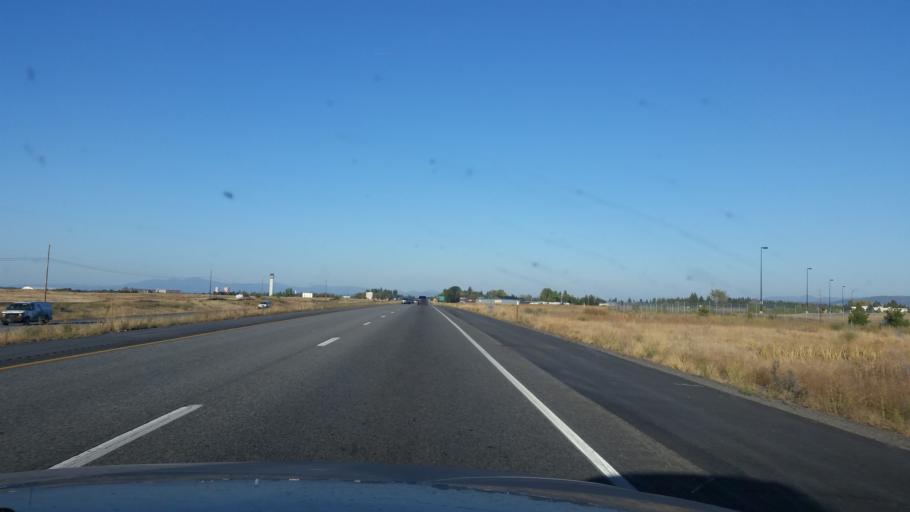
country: US
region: Washington
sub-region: Spokane County
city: Airway Heights
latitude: 47.5983
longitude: -117.5517
